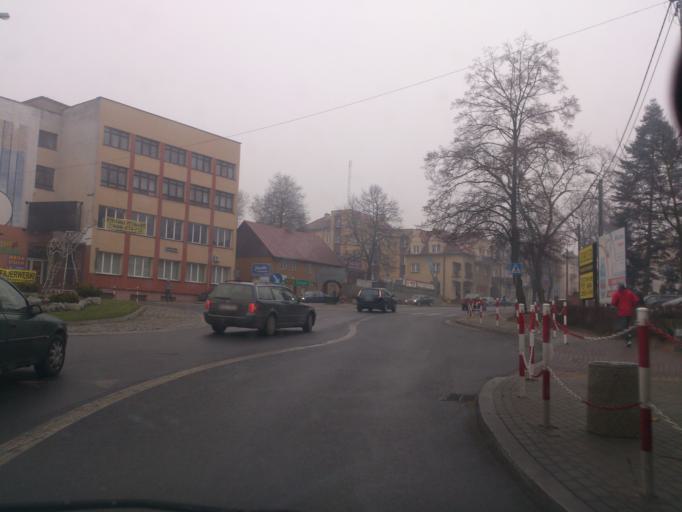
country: PL
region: Kujawsko-Pomorskie
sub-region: Powiat rypinski
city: Rypin
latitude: 53.0657
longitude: 19.4088
